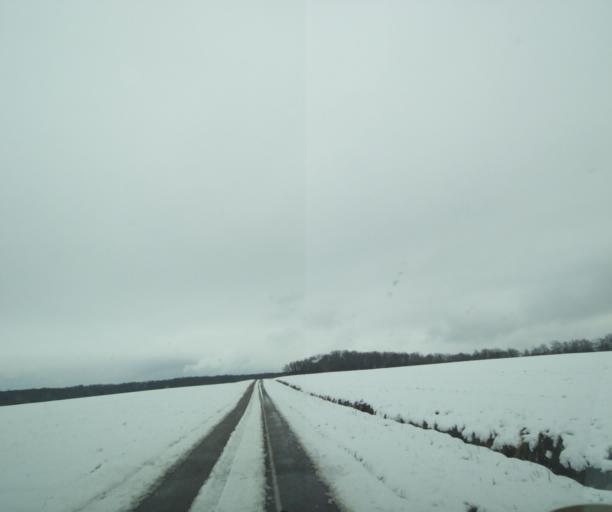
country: FR
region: Champagne-Ardenne
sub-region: Departement de la Haute-Marne
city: Montier-en-Der
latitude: 48.4155
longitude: 4.7457
